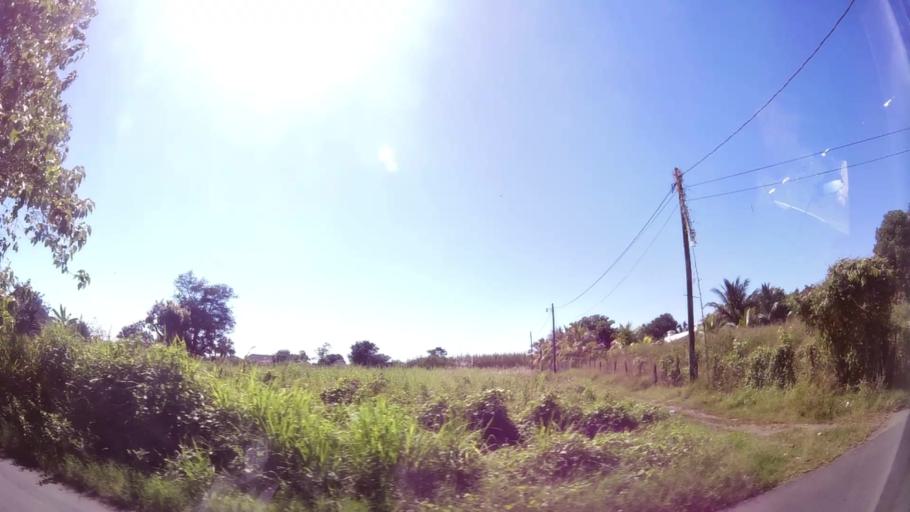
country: GT
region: Escuintla
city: Iztapa
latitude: 13.9329
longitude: -90.6853
